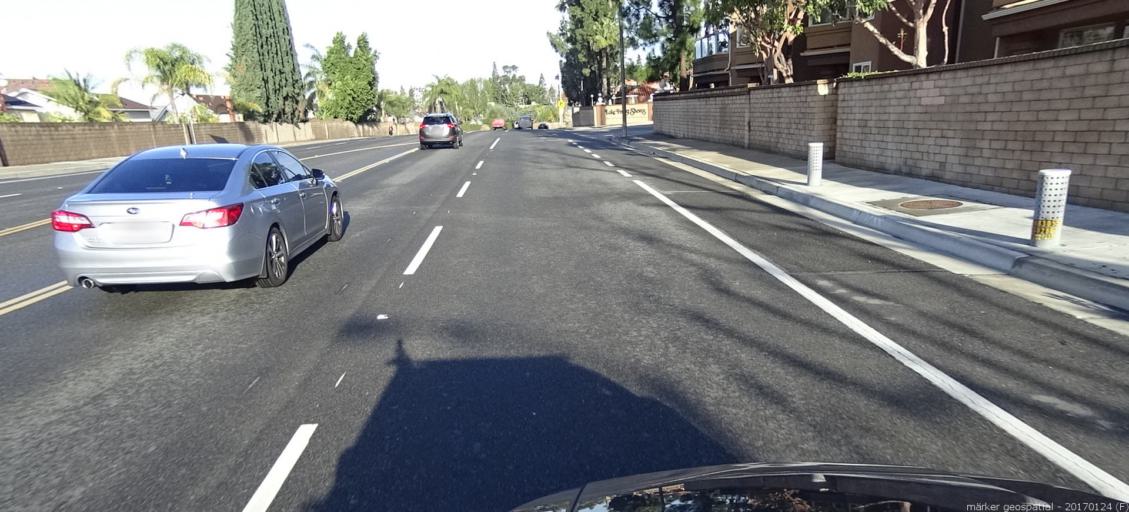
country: US
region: California
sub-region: Orange County
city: Laguna Hills
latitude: 33.6301
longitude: -117.7071
